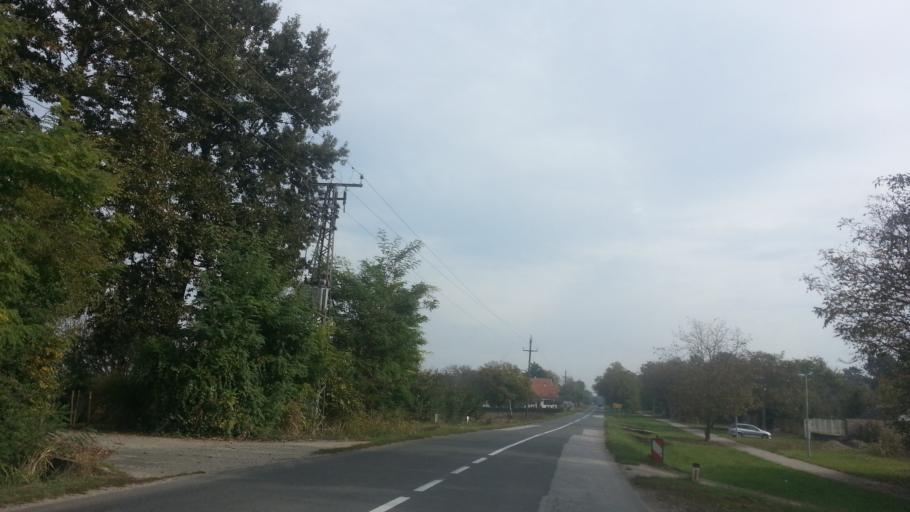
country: RS
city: Stari Banovci
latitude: 45.0015
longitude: 20.3032
